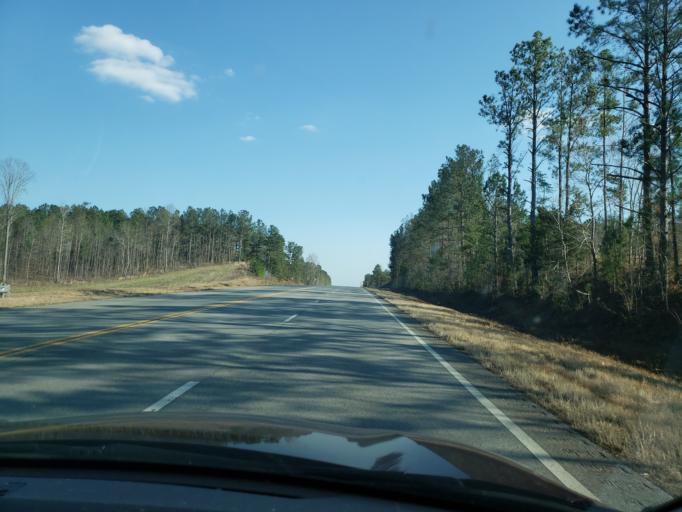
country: US
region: Alabama
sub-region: Randolph County
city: Wedowee
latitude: 33.4454
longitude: -85.5683
